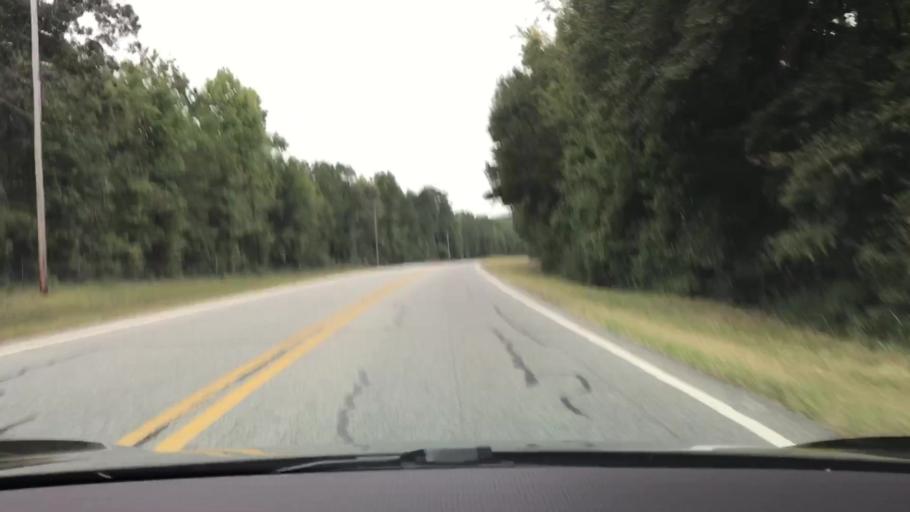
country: US
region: Georgia
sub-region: Oconee County
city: Watkinsville
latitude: 33.7589
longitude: -83.3075
